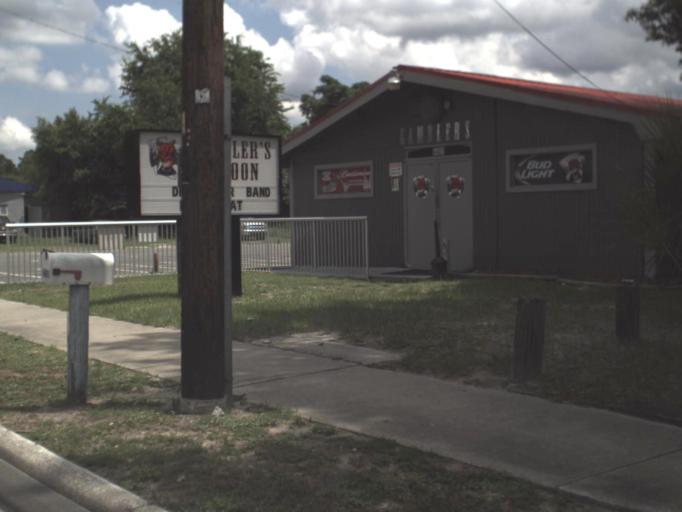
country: US
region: Florida
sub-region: Alachua County
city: Gainesville
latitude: 29.6951
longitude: -82.3348
